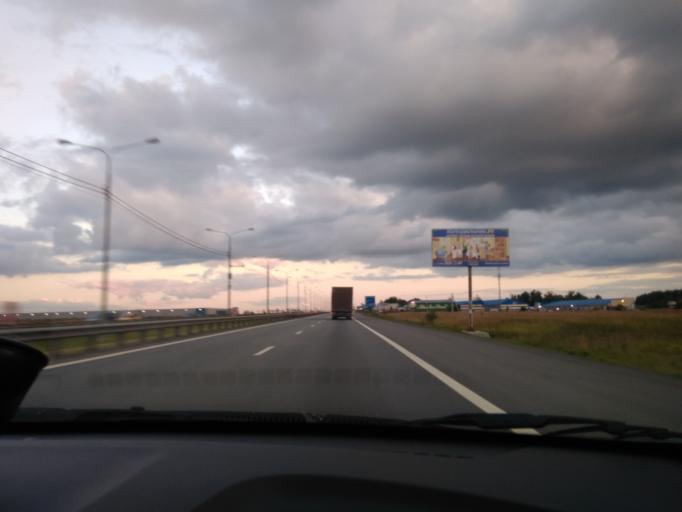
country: RU
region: Moskovskaya
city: Zhukovskiy
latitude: 55.4980
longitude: 38.1484
